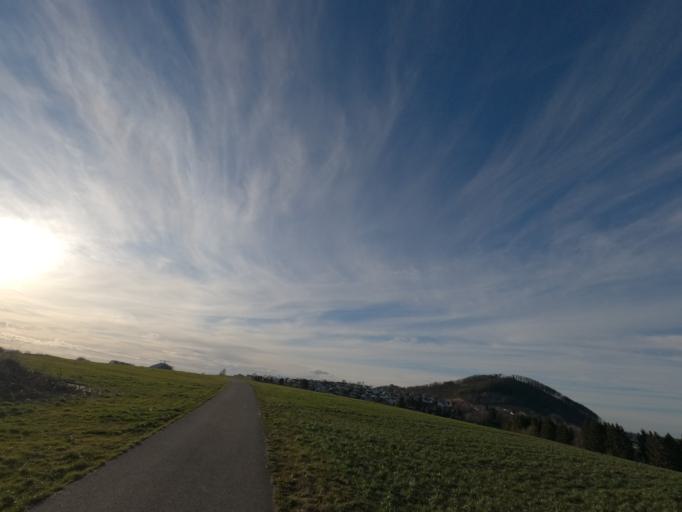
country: DE
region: Baden-Wuerttemberg
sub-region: Regierungsbezirk Stuttgart
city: Waldstetten
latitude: 48.7462
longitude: 9.8037
